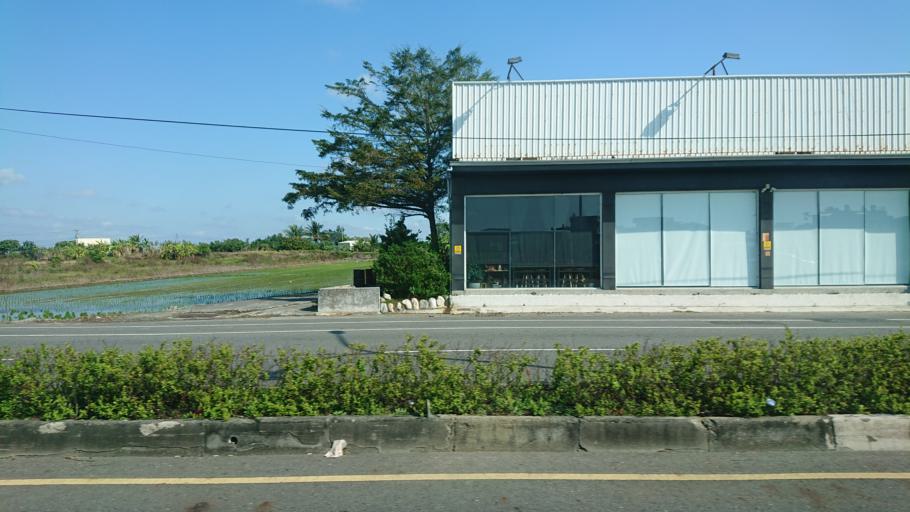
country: TW
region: Taiwan
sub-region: Chiayi
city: Taibao
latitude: 23.4400
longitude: 120.3820
